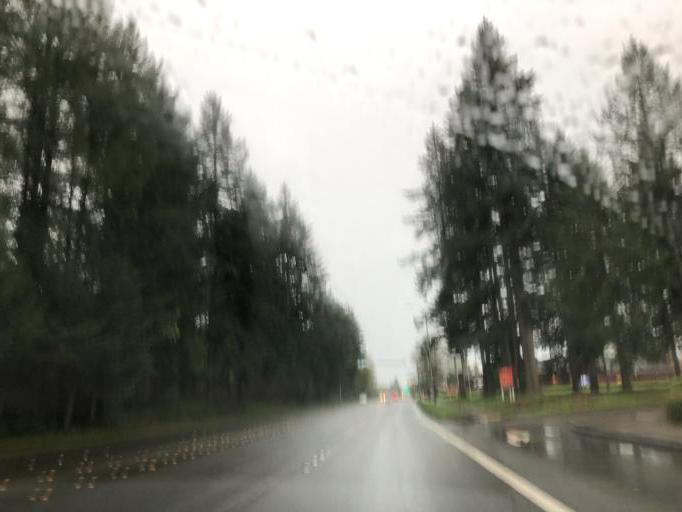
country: US
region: Washington
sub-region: Thurston County
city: Lacey
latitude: 47.0427
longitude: -122.8234
